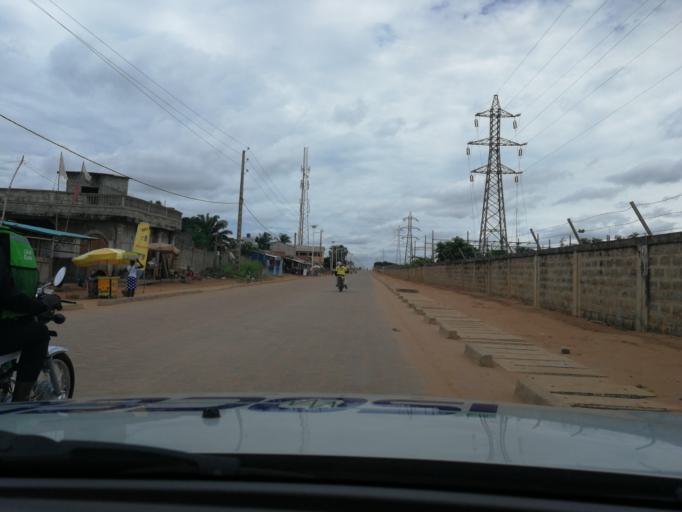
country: BJ
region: Atlantique
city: Abomey-Calavi
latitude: 6.4225
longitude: 2.3071
